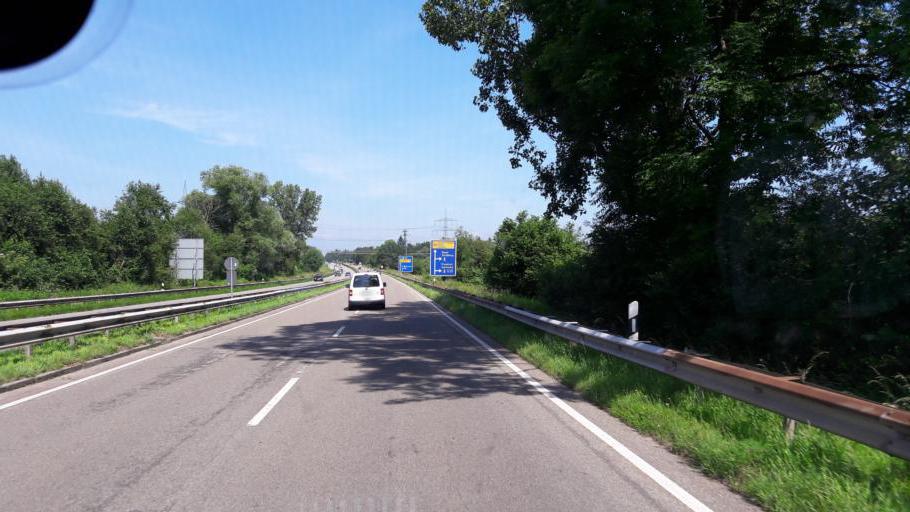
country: DE
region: Baden-Wuerttemberg
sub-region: Karlsruhe Region
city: Sinzheim
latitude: 48.7861
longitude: 8.1695
